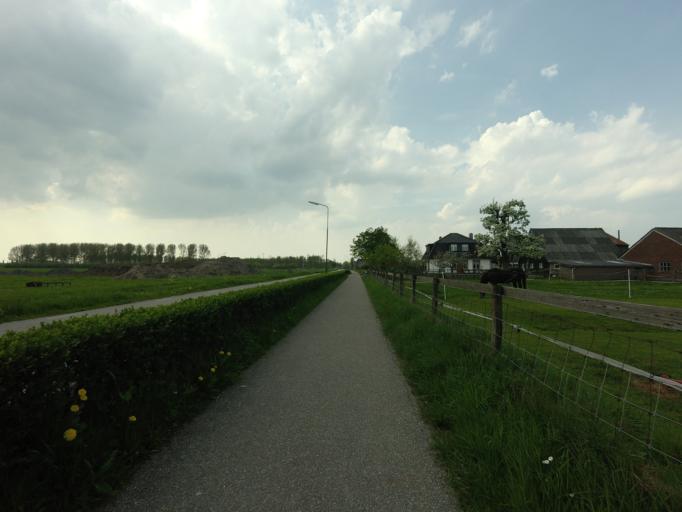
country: NL
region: Utrecht
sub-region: Gemeente Houten
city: Houten
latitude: 51.9947
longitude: 5.1563
